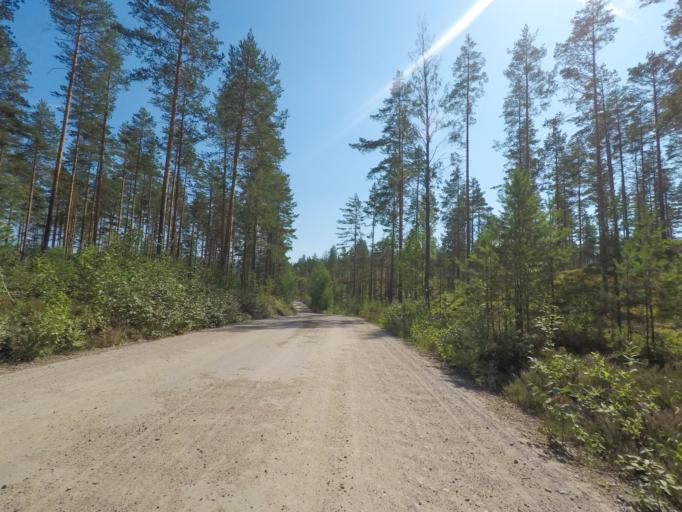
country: FI
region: Southern Savonia
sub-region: Mikkeli
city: Puumala
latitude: 61.4164
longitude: 28.0430
